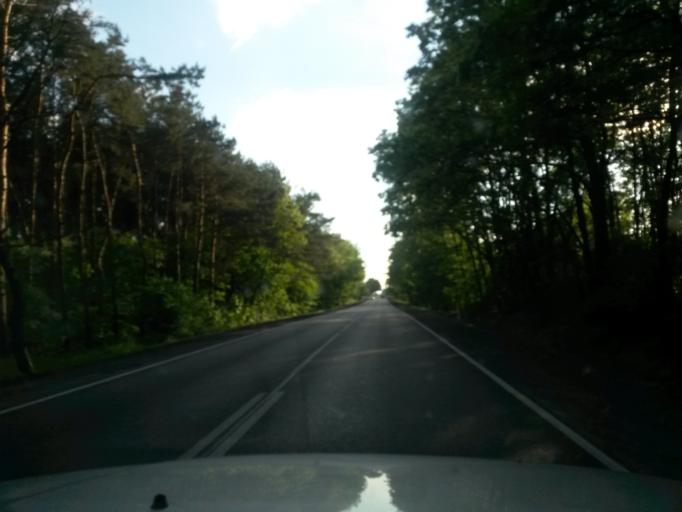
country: PL
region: Lodz Voivodeship
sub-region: Powiat belchatowski
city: Kluki
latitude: 51.3441
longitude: 19.2553
